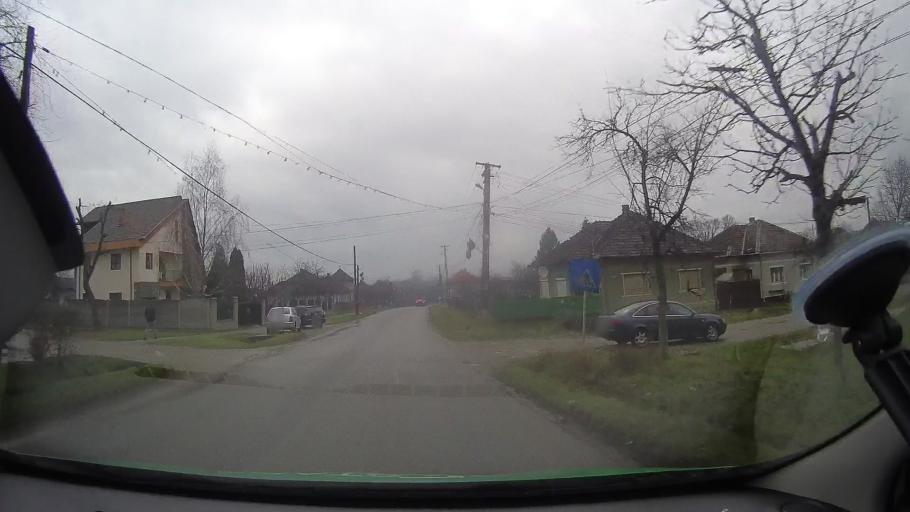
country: RO
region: Arad
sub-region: Comuna Gurahont
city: Gurahont
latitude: 46.2723
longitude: 22.3384
